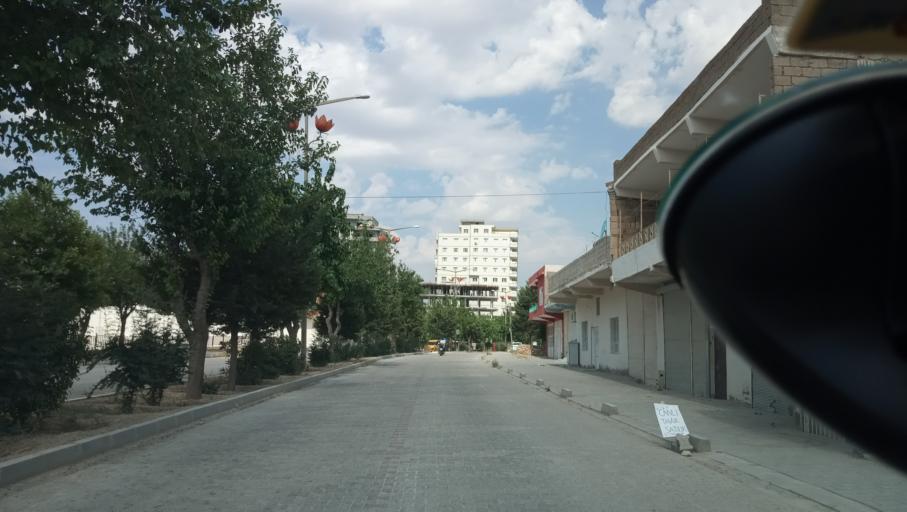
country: TR
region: Mardin
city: Yesilli
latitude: 37.3395
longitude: 40.8170
